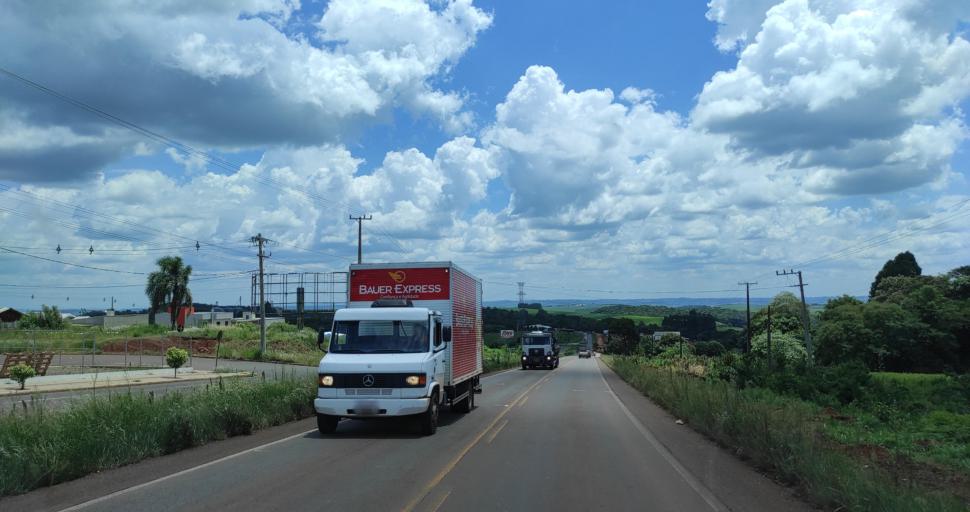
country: BR
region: Santa Catarina
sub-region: Xanxere
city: Xanxere
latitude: -26.8482
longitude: -52.4069
